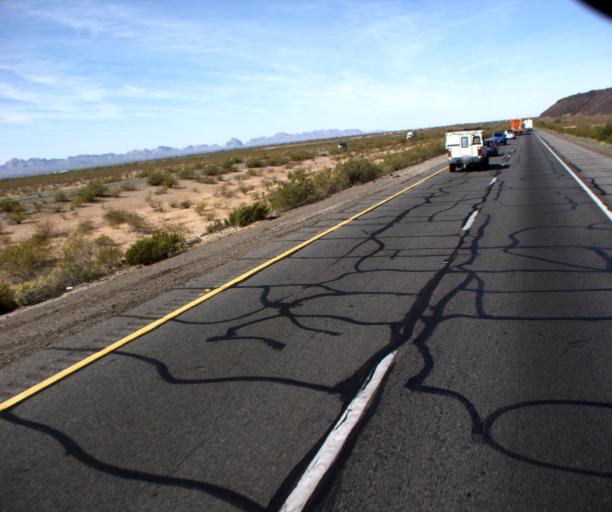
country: US
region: Arizona
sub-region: Maricopa County
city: Buckeye
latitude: 33.5249
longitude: -113.0934
